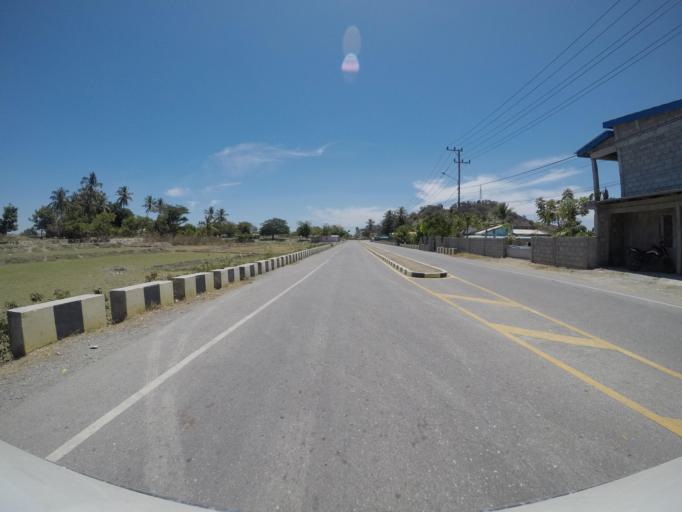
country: TL
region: Manatuto
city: Manatuto
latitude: -8.5205
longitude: 126.0067
